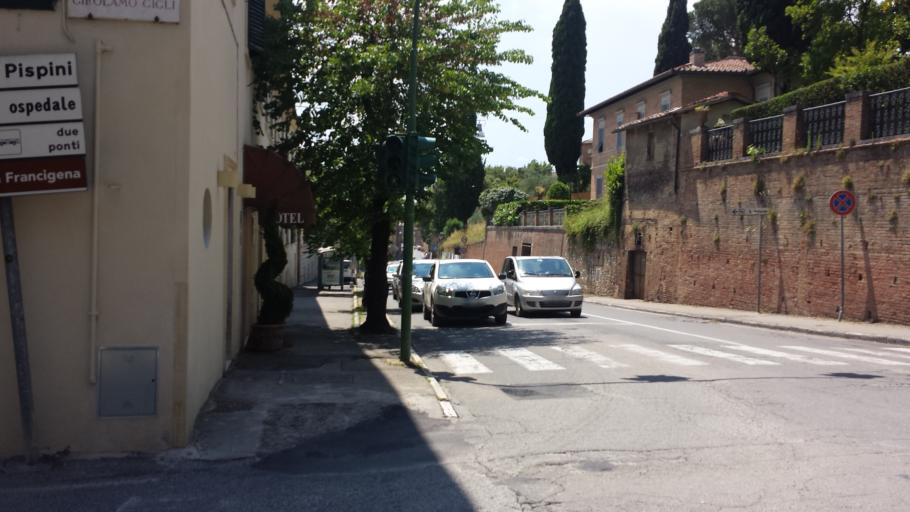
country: IT
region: Tuscany
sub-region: Provincia di Siena
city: Siena
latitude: 43.3117
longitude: 11.3394
